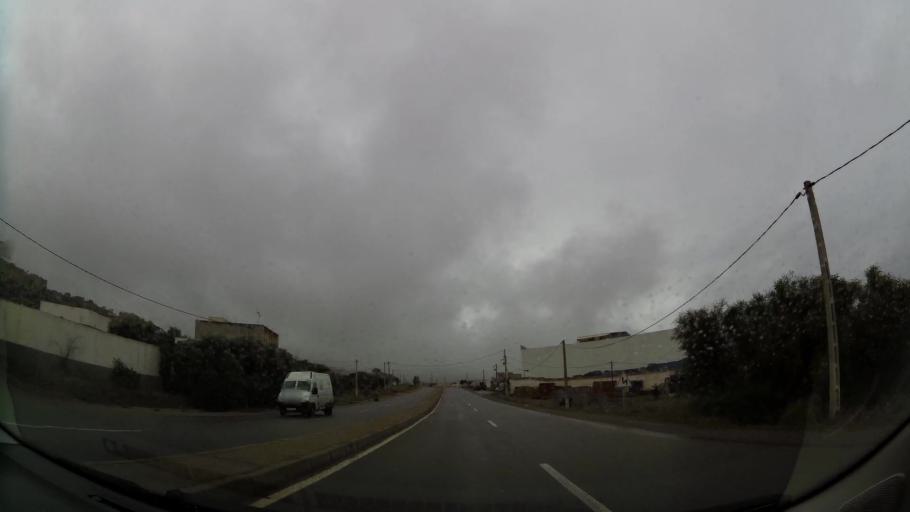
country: MA
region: Taza-Al Hoceima-Taounate
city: Imzourene
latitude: 35.1919
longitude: -3.8892
